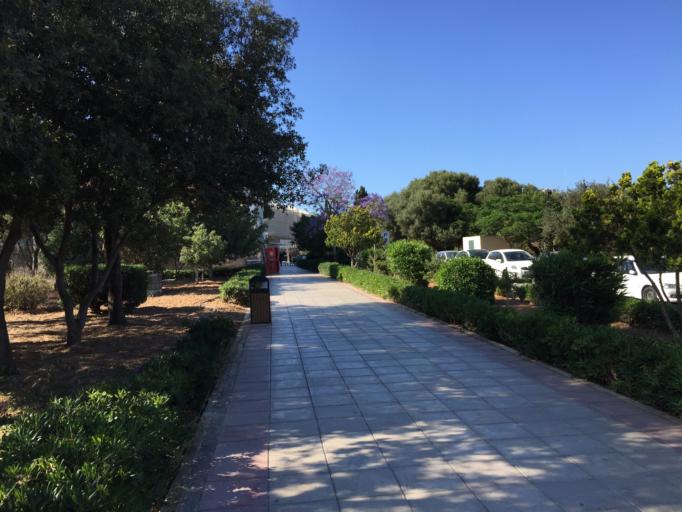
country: MT
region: Il-Gzira
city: Gzira
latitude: 35.9012
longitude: 14.4836
